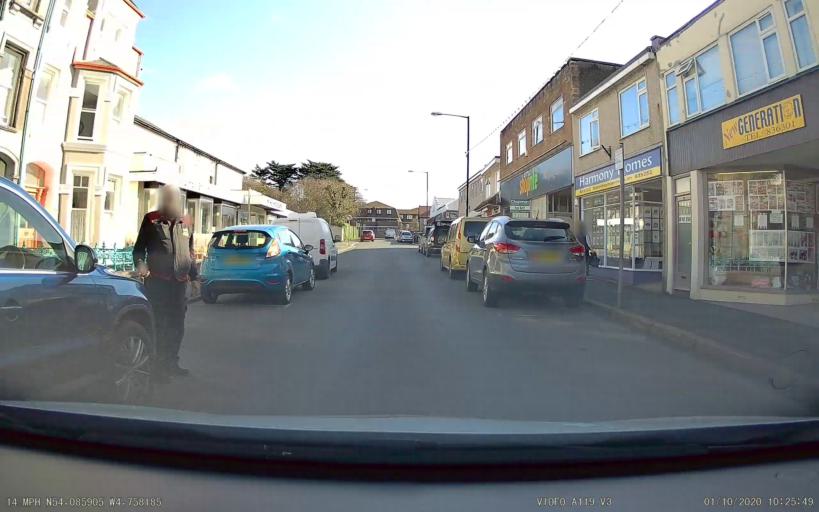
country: IM
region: Port Erin
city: Port Erin
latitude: 54.0859
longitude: -4.7582
